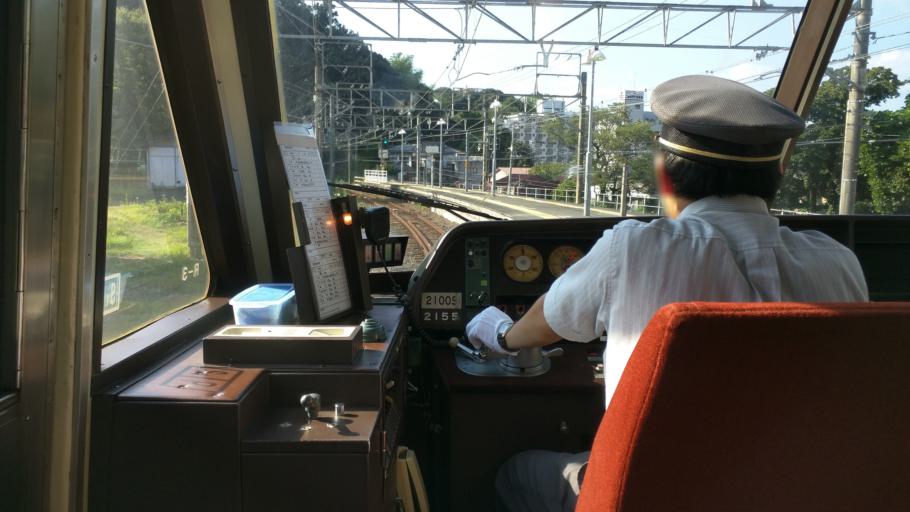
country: JP
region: Shizuoka
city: Atami
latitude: 35.0440
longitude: 139.0811
